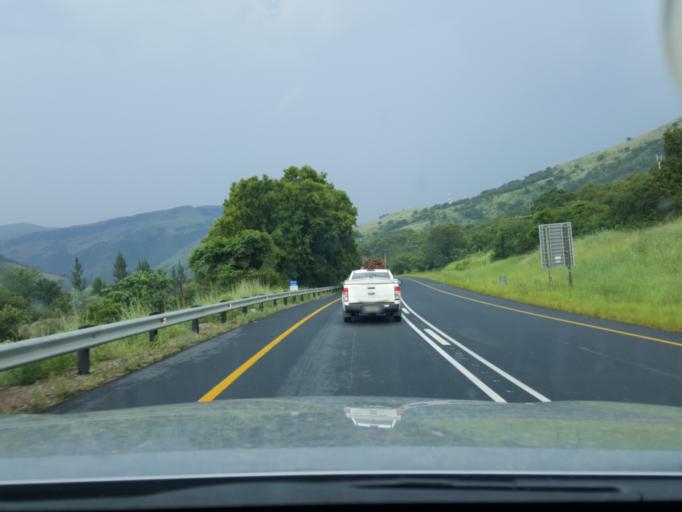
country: ZA
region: Mpumalanga
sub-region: Nkangala District Municipality
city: Belfast
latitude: -25.6333
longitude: 30.3945
